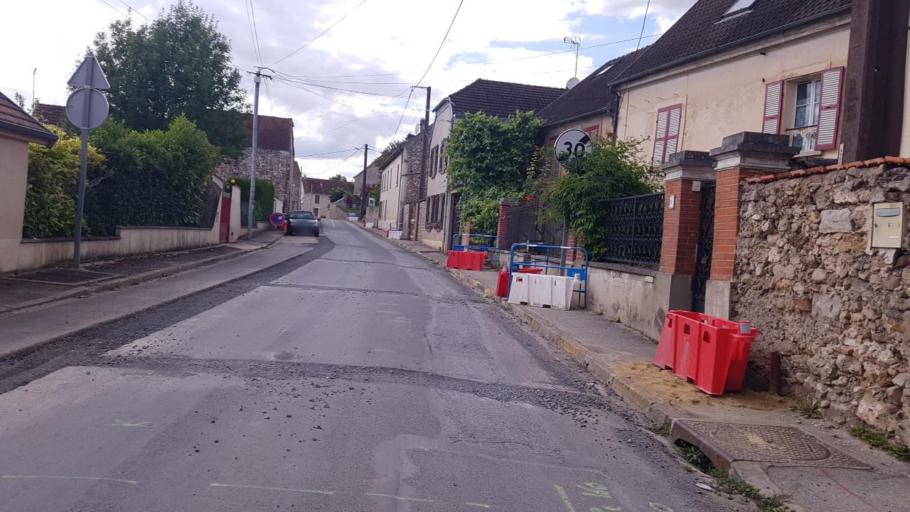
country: FR
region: Picardie
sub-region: Departement de l'Aisne
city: Crezancy
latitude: 49.0755
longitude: 3.5031
